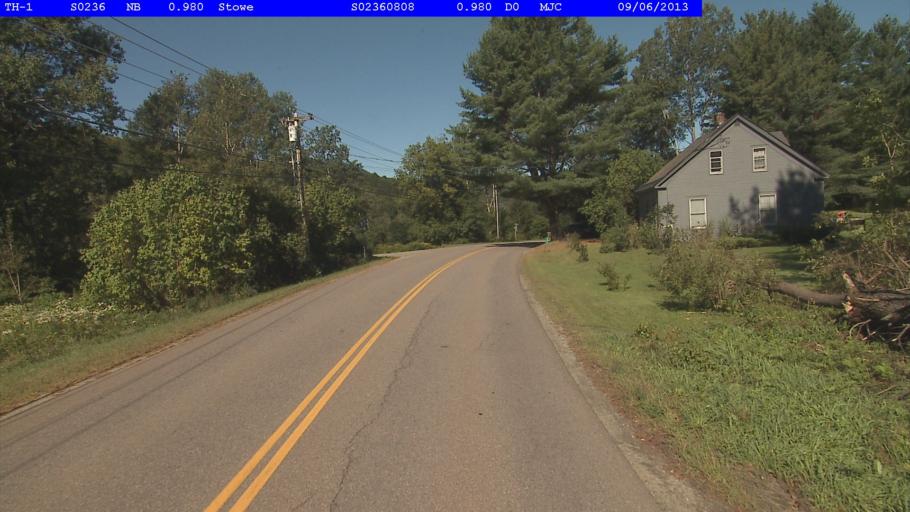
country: US
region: Vermont
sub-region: Washington County
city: Waterbury
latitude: 44.4432
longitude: -72.7252
